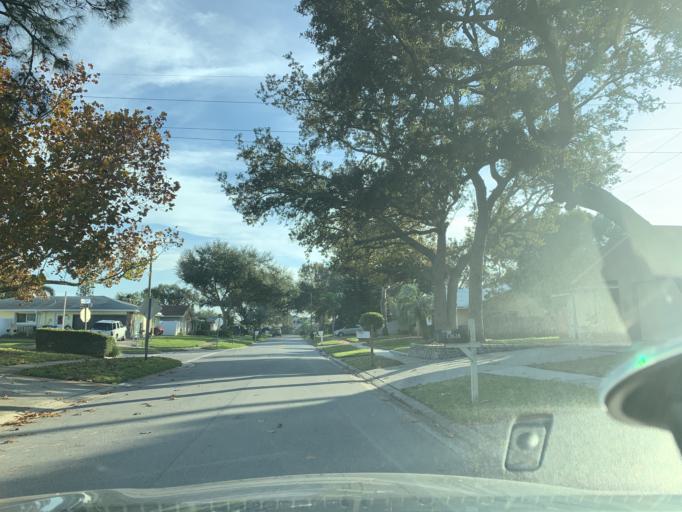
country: US
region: Florida
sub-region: Pinellas County
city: Ridgecrest
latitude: 27.8880
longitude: -82.7990
